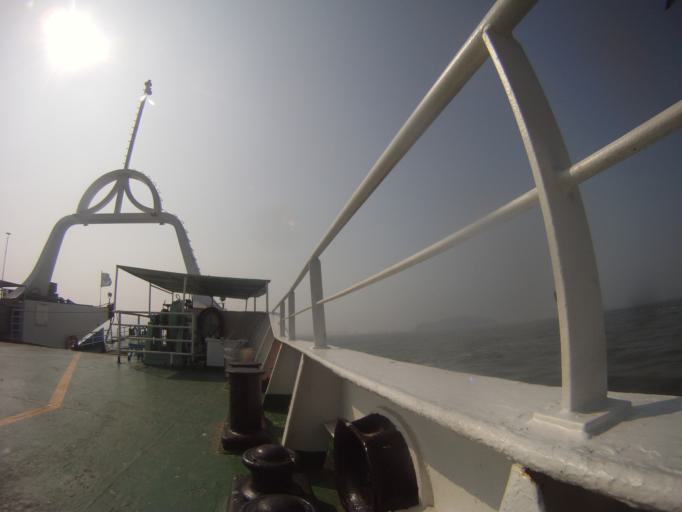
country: KR
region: Incheon
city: Incheon
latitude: 37.4912
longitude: 126.5884
